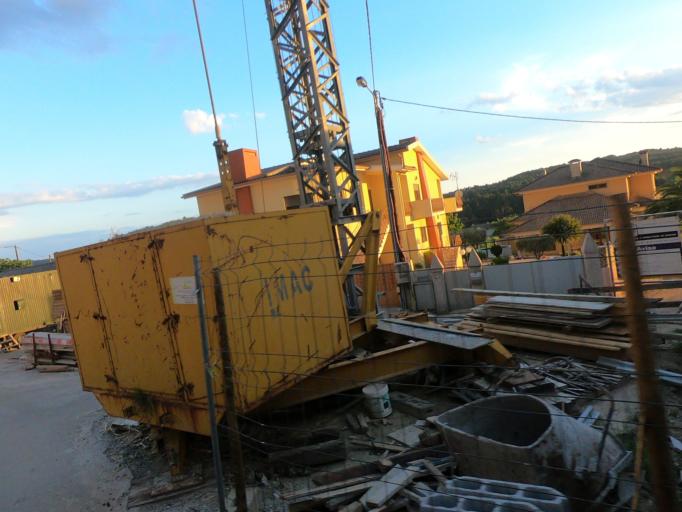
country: PT
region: Vila Real
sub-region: Vila Real
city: Vila Real
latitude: 41.2648
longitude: -7.6880
